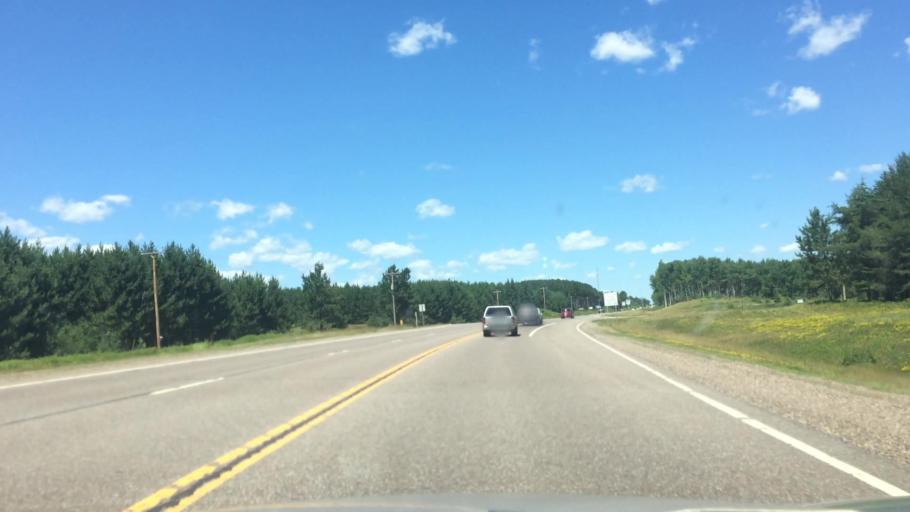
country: US
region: Wisconsin
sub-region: Lincoln County
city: Tomahawk
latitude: 45.6653
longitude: -89.7138
